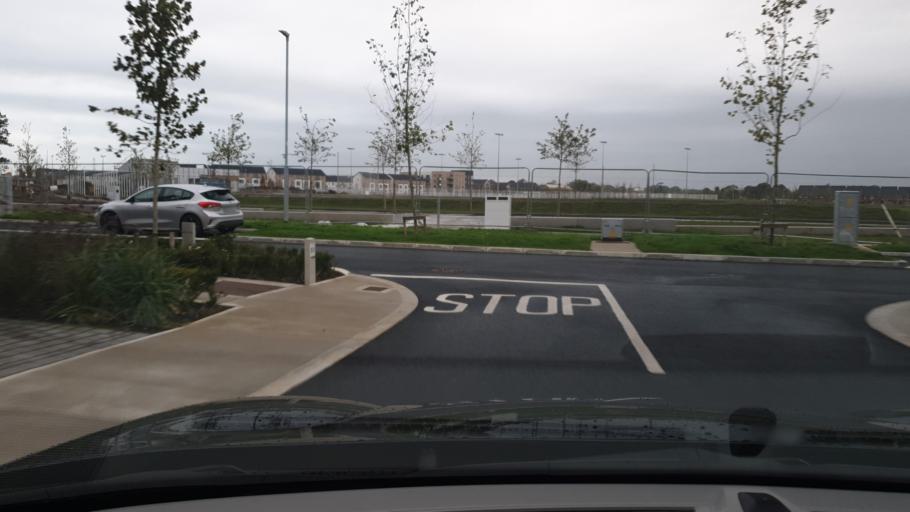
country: IE
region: Leinster
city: Lucan
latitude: 53.3448
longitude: -6.4678
